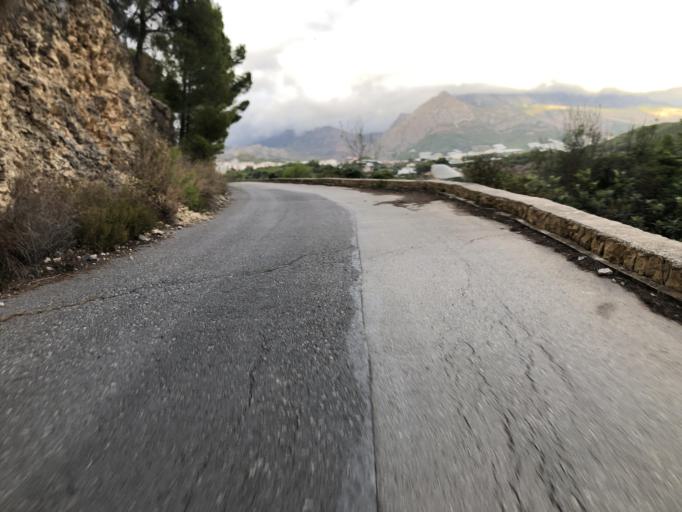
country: ES
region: Valencia
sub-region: Provincia de Alicante
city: Polop
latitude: 38.6383
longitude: -0.1347
